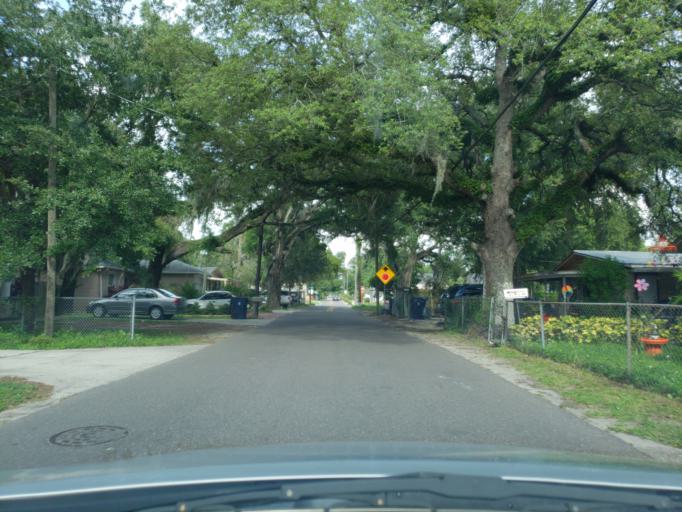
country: US
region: Florida
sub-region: Hillsborough County
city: East Lake-Orient Park
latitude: 27.9851
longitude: -82.4234
